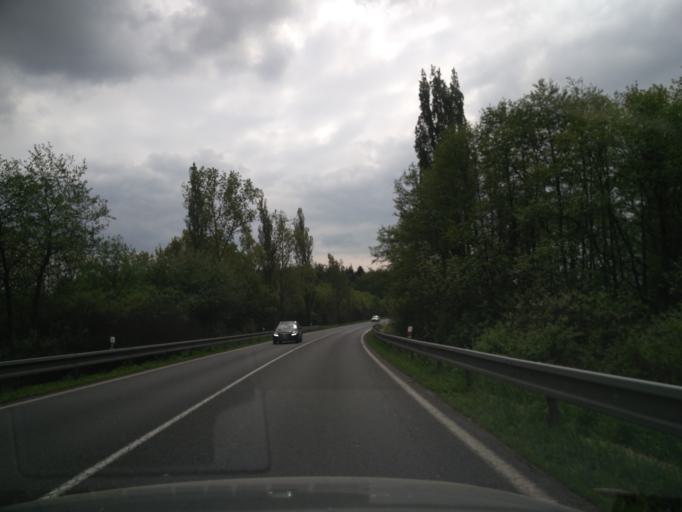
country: CZ
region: Central Bohemia
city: Milin
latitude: 49.5889
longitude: 14.0715
